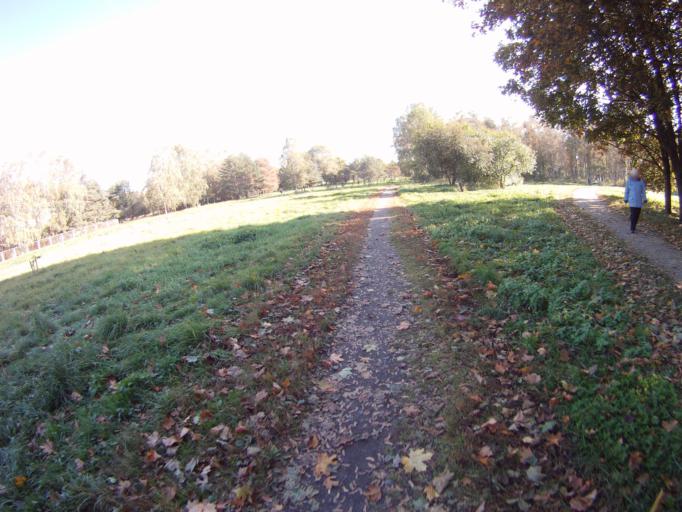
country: BY
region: Minsk
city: Minsk
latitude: 53.9341
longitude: 27.5709
